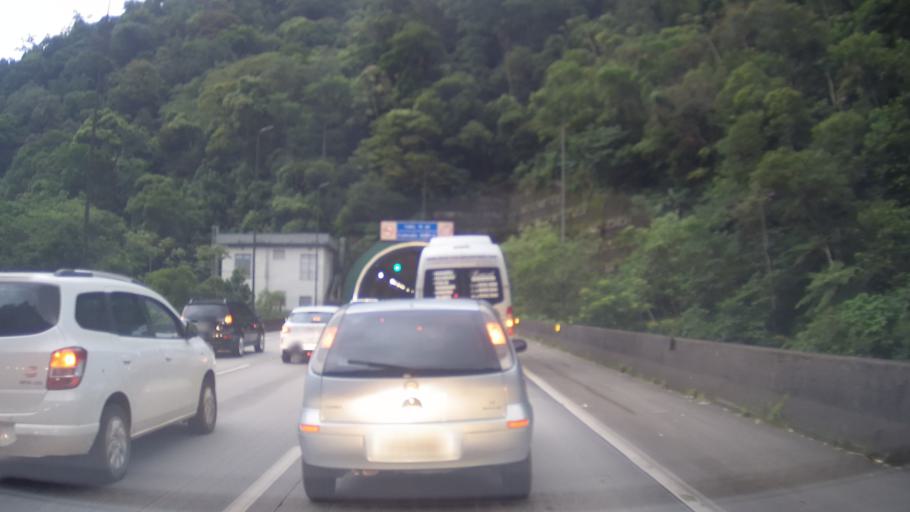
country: BR
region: Sao Paulo
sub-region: Cubatao
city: Cubatao
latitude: -23.8834
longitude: -46.4944
